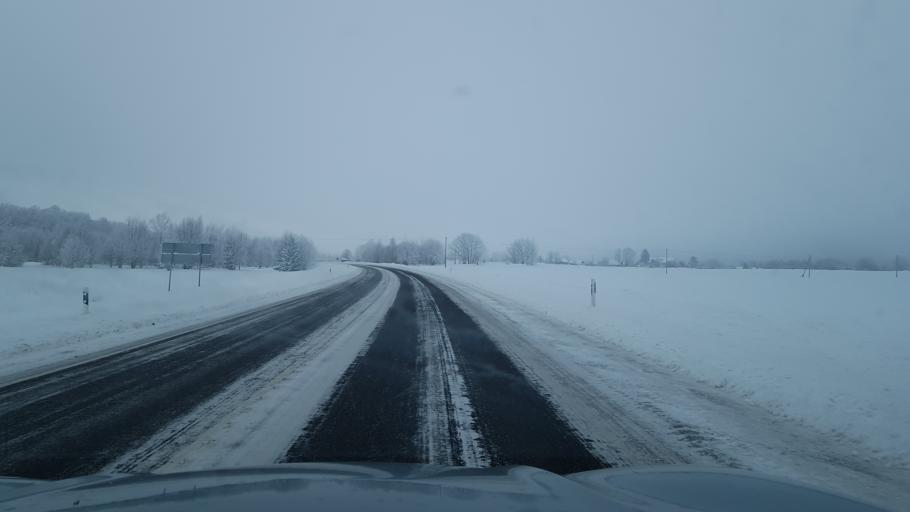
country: EE
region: Ida-Virumaa
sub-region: Johvi vald
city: Johvi
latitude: 59.2534
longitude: 27.3804
